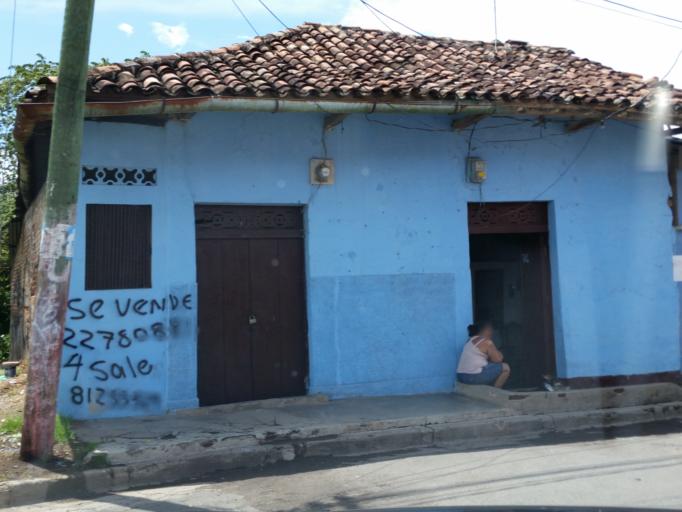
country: NI
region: Granada
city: Granada
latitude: 11.9335
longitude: -85.9568
